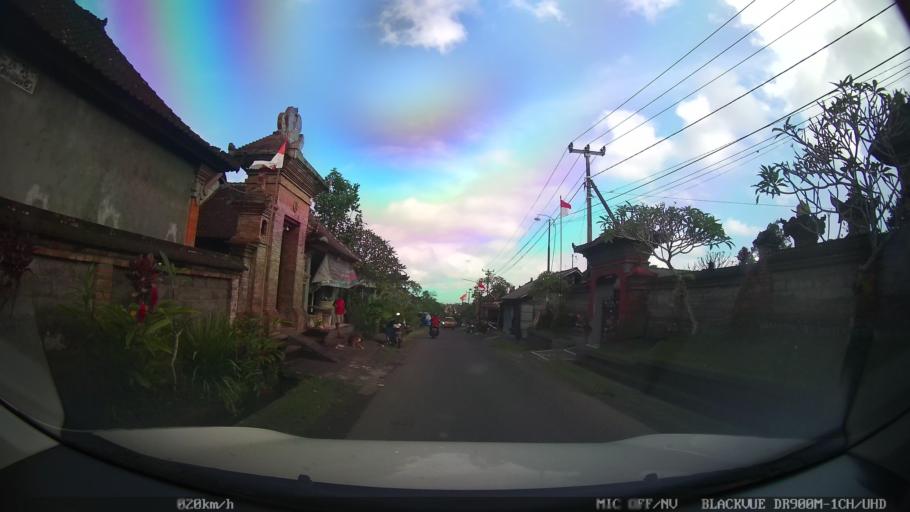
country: ID
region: Bali
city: Banjar Pesalakan
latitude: -8.4907
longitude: 115.2979
